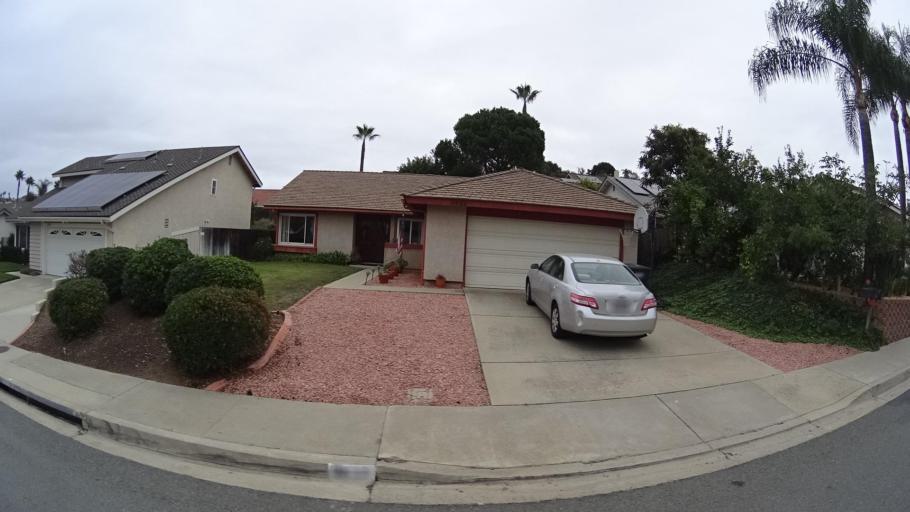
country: US
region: California
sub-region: San Diego County
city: Rancho San Diego
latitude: 32.7542
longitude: -116.9181
